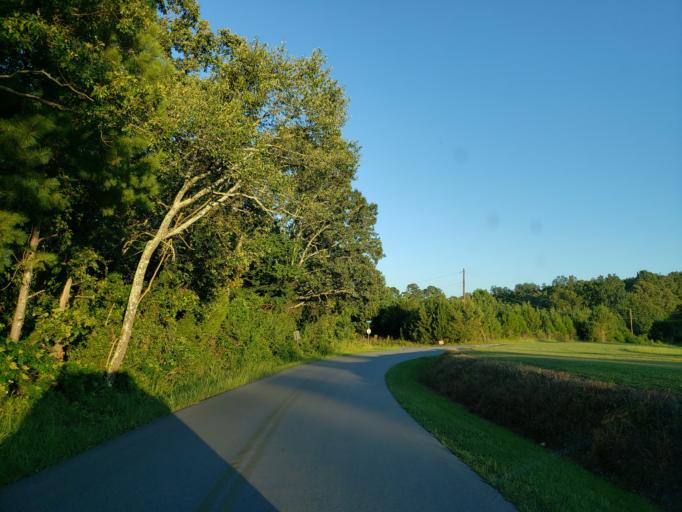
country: US
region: Georgia
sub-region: Bartow County
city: Euharlee
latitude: 34.0812
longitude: -84.9270
